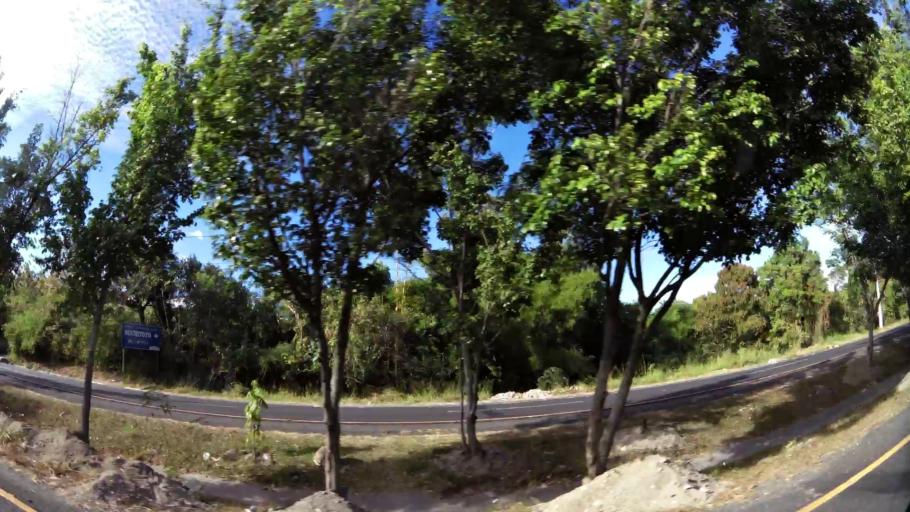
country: SV
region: Cuscatlan
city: Tecoluca
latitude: 13.7371
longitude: -89.0427
